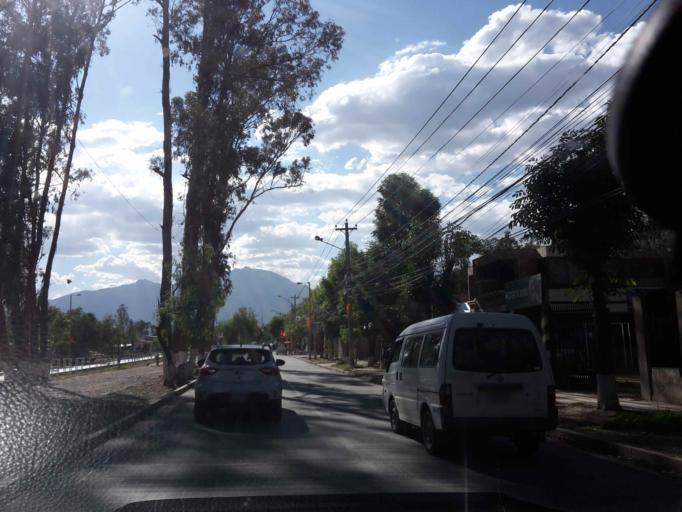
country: BO
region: Cochabamba
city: Cochabamba
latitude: -17.3430
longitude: -66.2093
